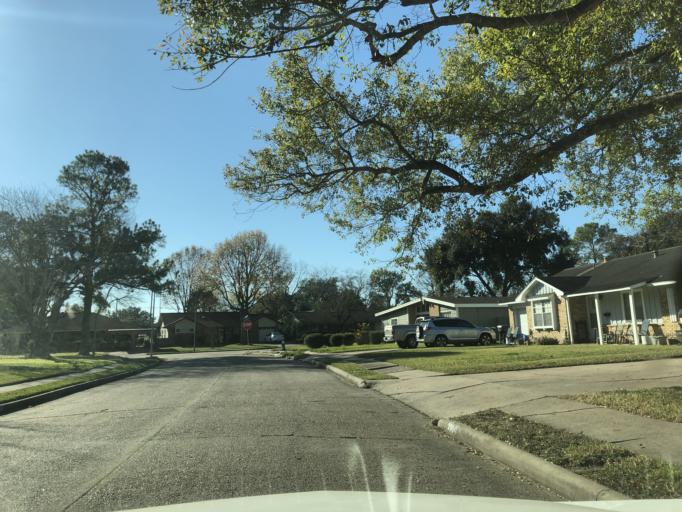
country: US
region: Texas
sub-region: Harris County
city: Bellaire
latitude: 29.6947
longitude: -95.5095
